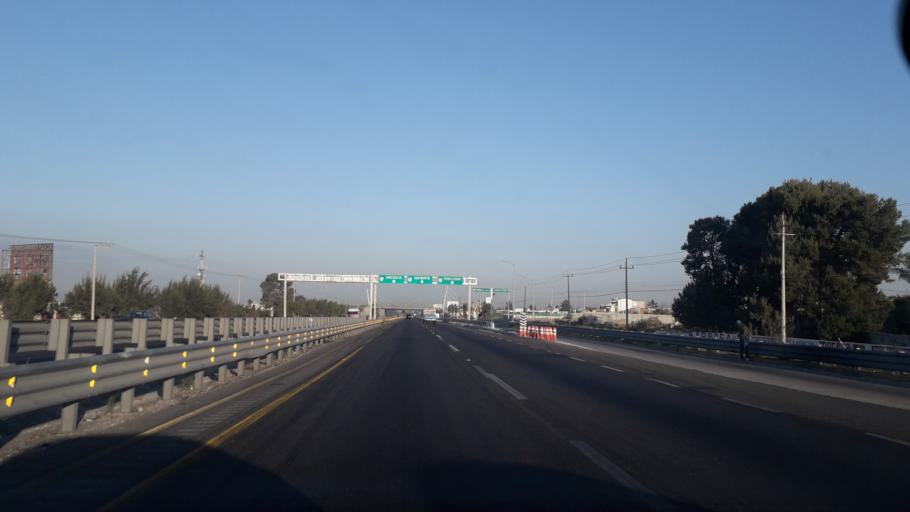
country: MX
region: Puebla
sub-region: Puebla
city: Primero de Mayo
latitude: 19.0665
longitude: -98.1137
